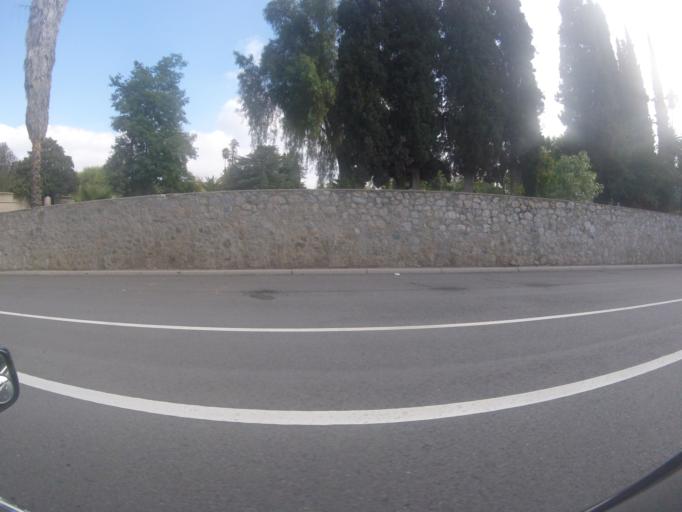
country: US
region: California
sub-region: San Bernardino County
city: Redlands
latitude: 34.0343
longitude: -117.1871
